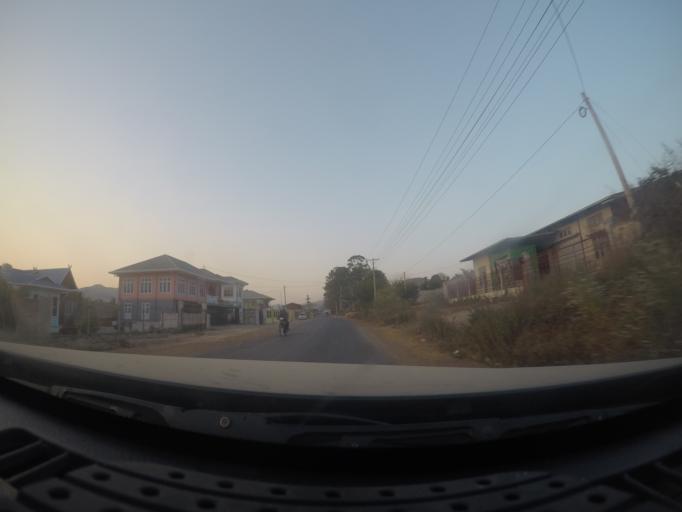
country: MM
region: Shan
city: Taunggyi
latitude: 20.7069
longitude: 97.0587
